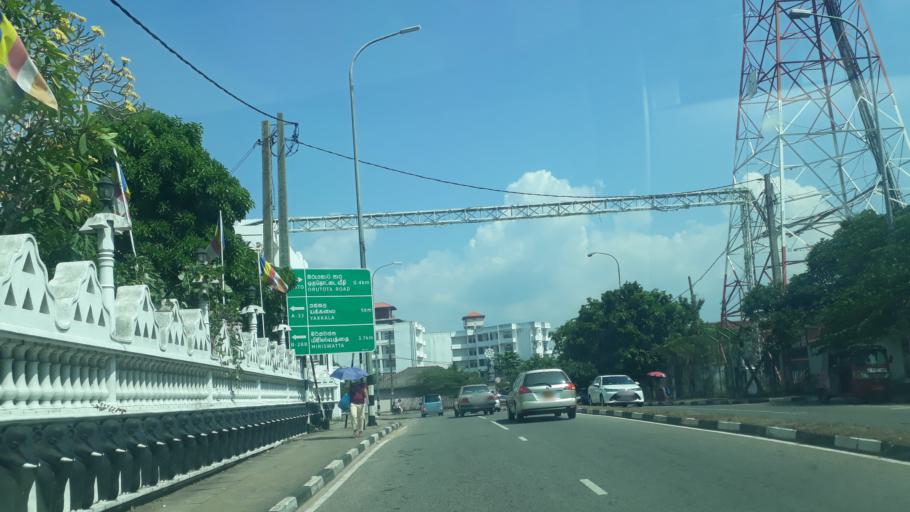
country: LK
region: Western
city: Gampaha
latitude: 7.0911
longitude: 79.9921
